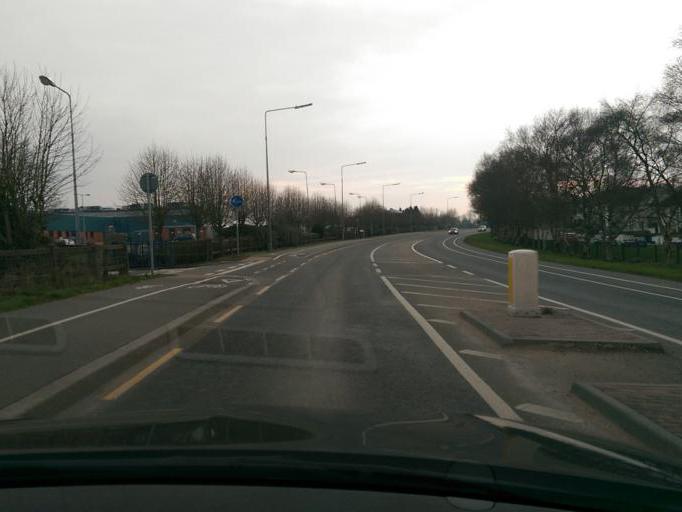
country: IE
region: Leinster
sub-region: An Iarmhi
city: Athlone
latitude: 53.4343
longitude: -7.9045
